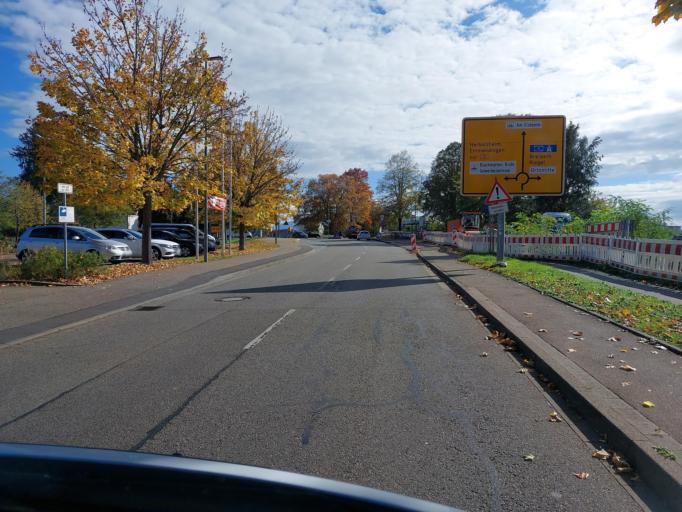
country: DE
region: Baden-Wuerttemberg
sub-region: Freiburg Region
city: Teningen
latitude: 48.1299
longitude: 7.8113
